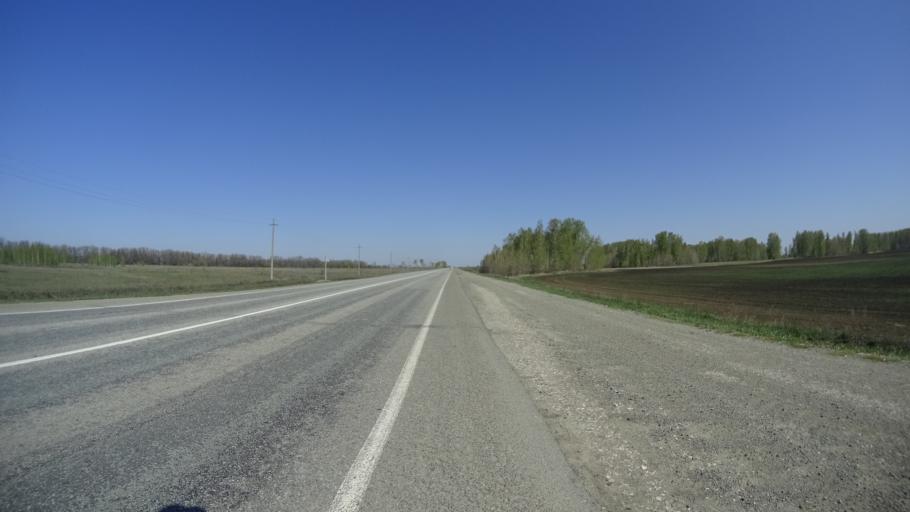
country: RU
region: Chelyabinsk
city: Troitsk
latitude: 54.1889
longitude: 61.4337
